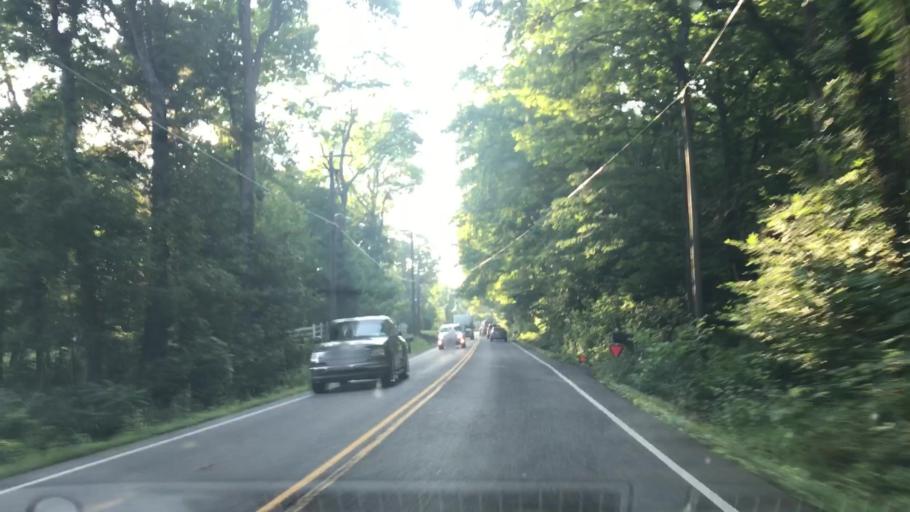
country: US
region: Tennessee
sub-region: Williamson County
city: Nolensville
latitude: 35.9910
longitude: -86.6445
